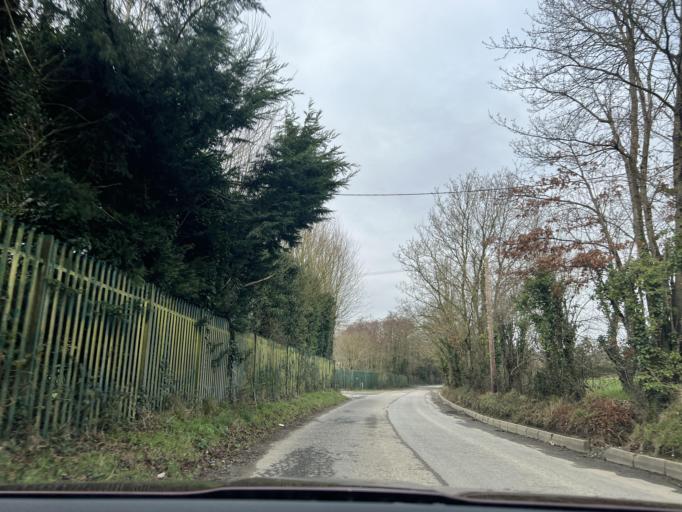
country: IE
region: Leinster
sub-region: Loch Garman
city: Castlebridge
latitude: 52.3832
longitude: -6.5624
